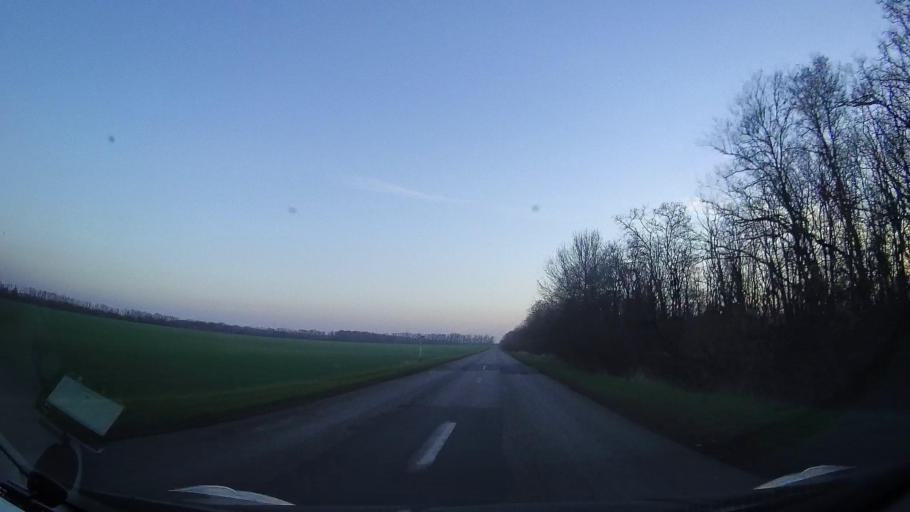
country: RU
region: Rostov
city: Zernograd
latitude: 46.9727
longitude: 40.3915
